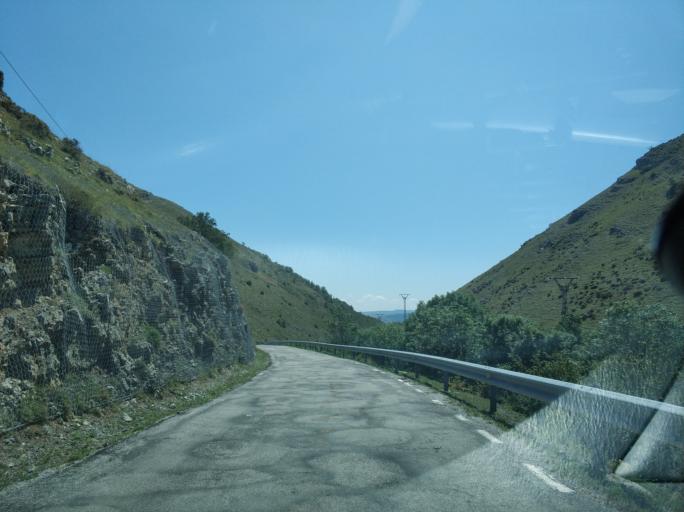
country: ES
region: Cantabria
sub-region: Provincia de Cantabria
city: Reinosa
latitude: 43.0305
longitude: -4.1704
